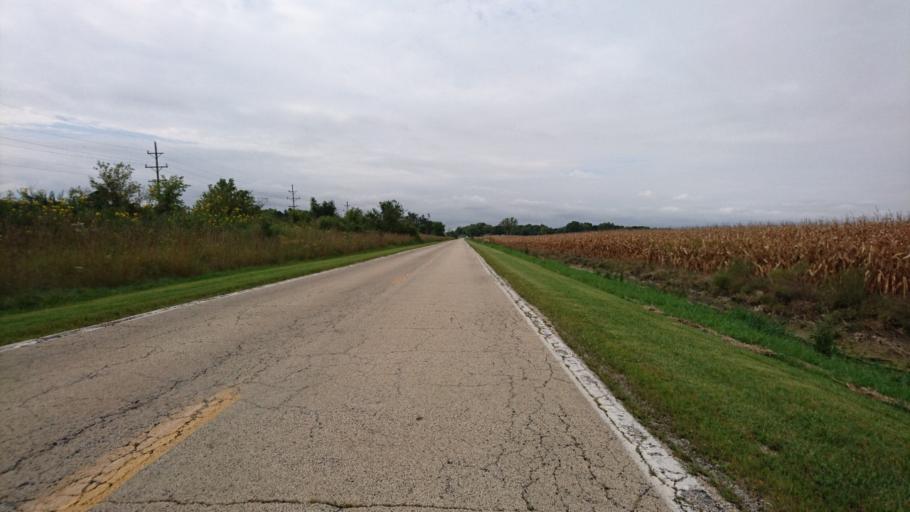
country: US
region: Illinois
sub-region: Livingston County
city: Odell
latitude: 41.0123
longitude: -88.5168
